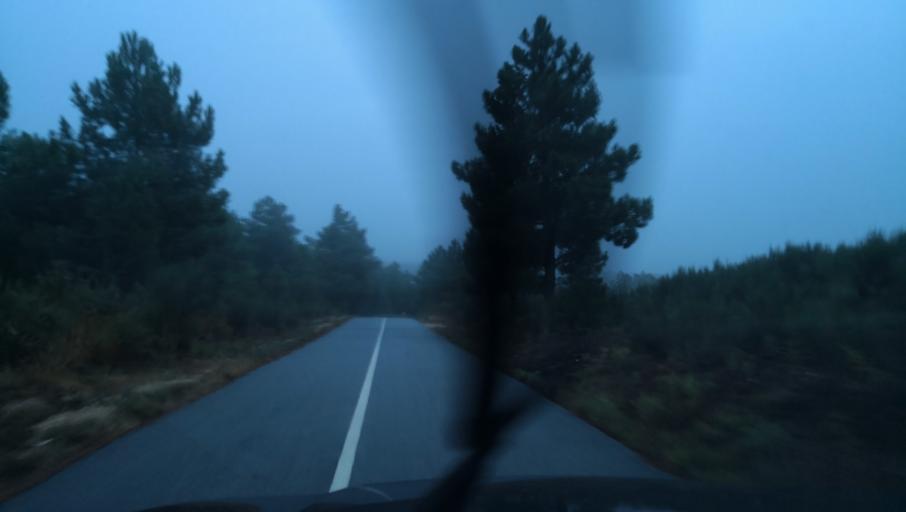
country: PT
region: Vila Real
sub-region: Sabrosa
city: Sabrosa
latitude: 41.2789
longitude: -7.5967
